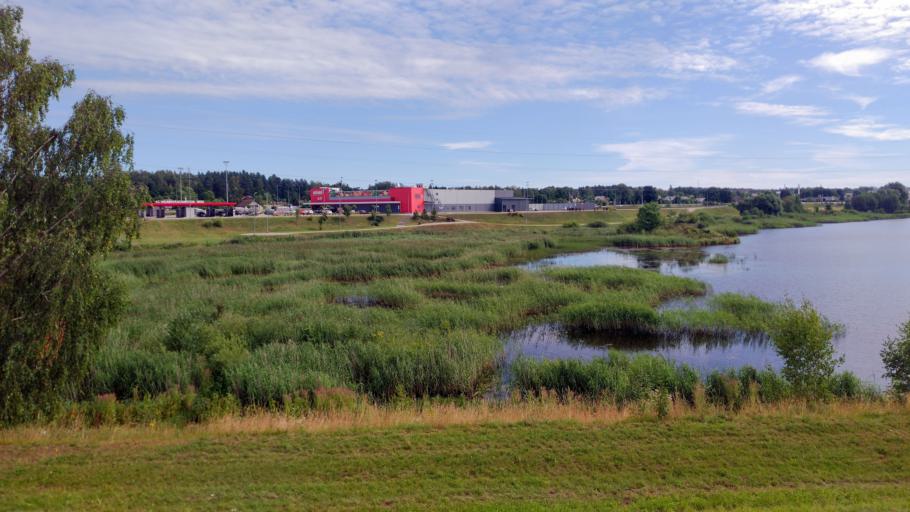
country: LV
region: Ogre
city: Ogre
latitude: 56.8158
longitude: 24.5735
